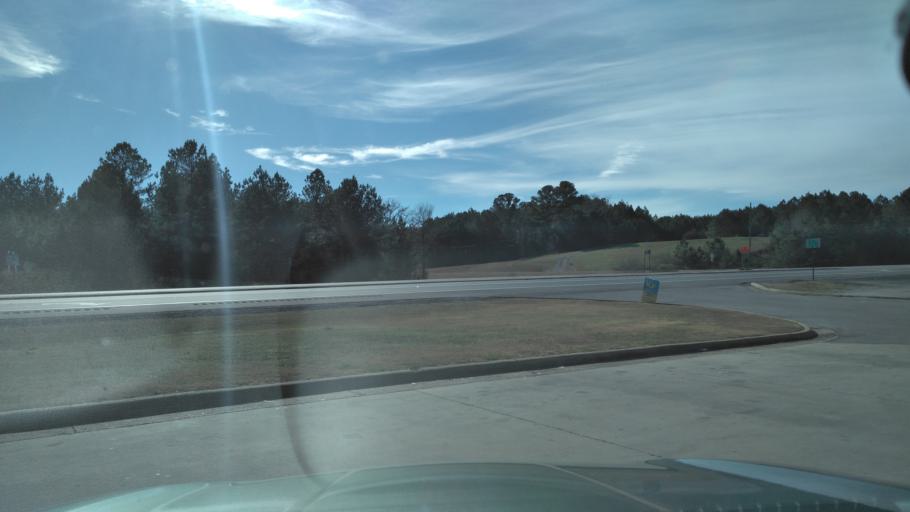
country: US
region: Alabama
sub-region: Walker County
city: Jasper
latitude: 33.8554
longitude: -87.3364
